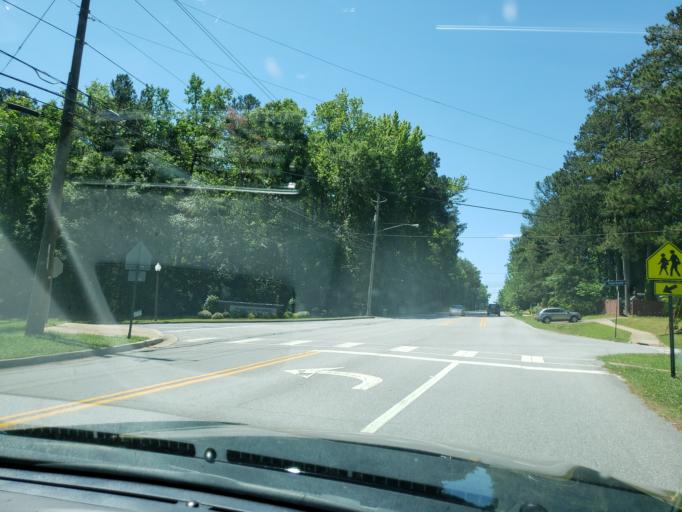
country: US
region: Alabama
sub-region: Lee County
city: Auburn
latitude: 32.6329
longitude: -85.4820
